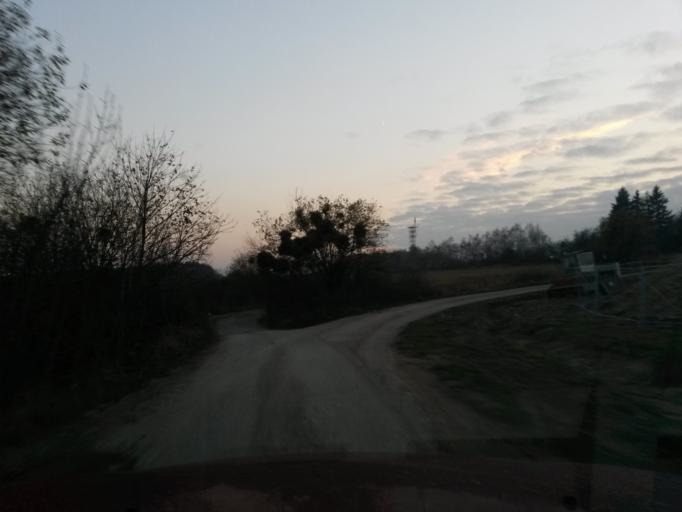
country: SK
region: Kosicky
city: Kosice
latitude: 48.7178
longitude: 21.2937
